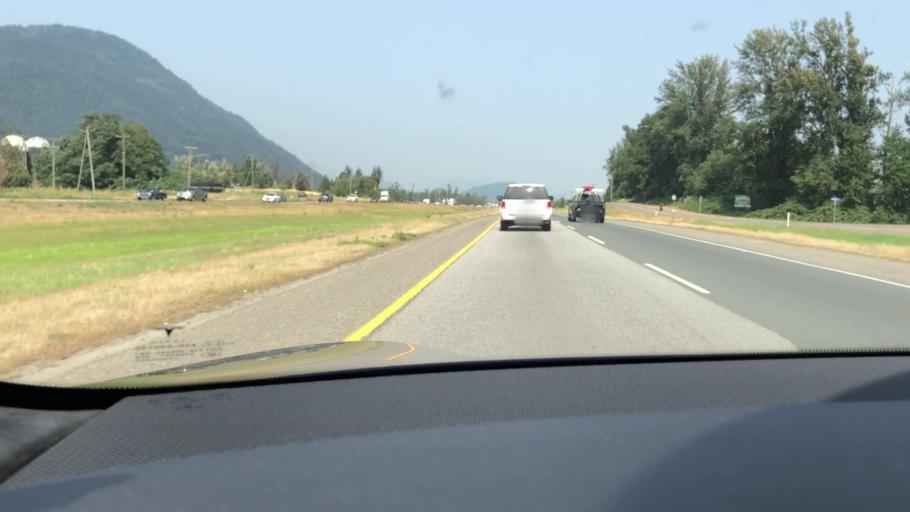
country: CA
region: British Columbia
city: Abbotsford
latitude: 49.0662
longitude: -122.1622
